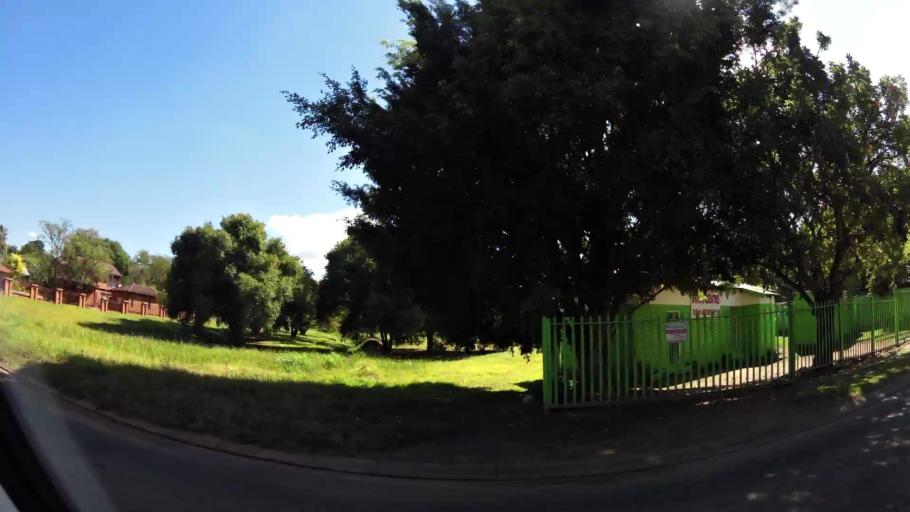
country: ZA
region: Limpopo
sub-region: Mopani District Municipality
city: Tzaneen
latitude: -23.8168
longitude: 30.1555
